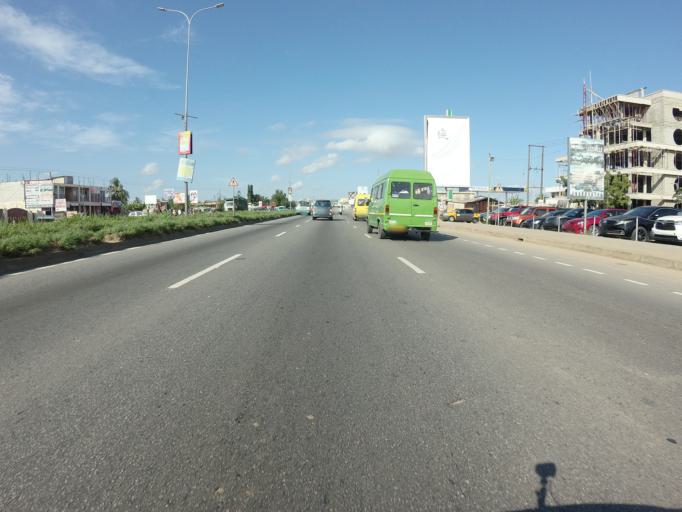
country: GH
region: Greater Accra
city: Gbawe
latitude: 5.5492
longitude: -0.3344
